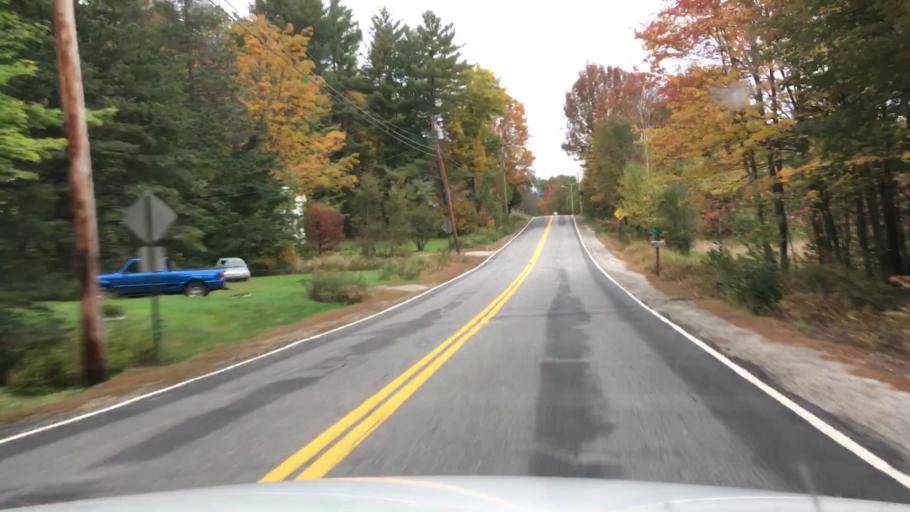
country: US
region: Maine
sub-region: Oxford County
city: Bethel
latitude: 44.4002
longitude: -70.7943
